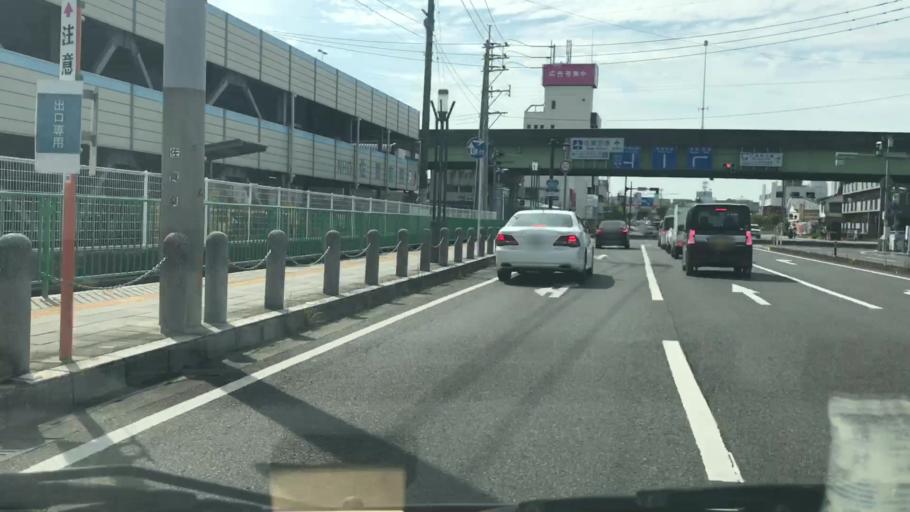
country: JP
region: Saga Prefecture
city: Saga-shi
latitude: 33.2751
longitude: 130.2936
